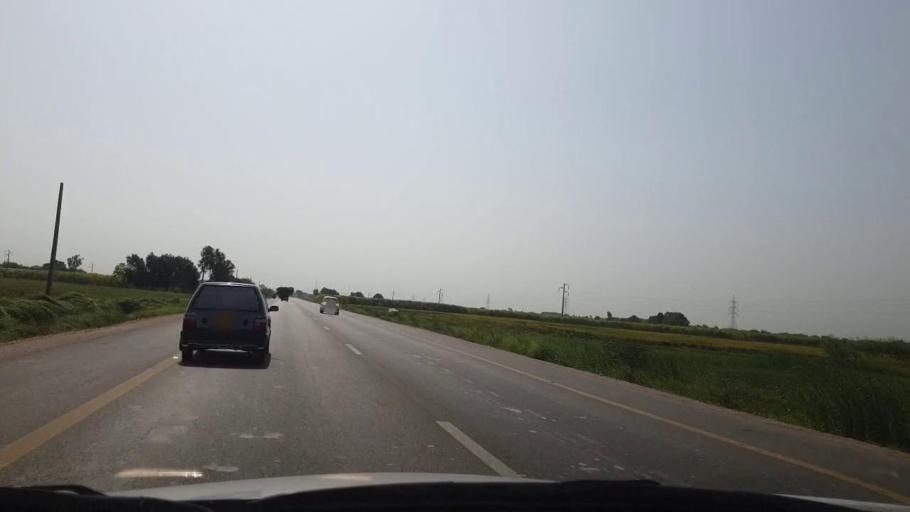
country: PK
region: Sindh
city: Tando Muhammad Khan
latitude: 25.1119
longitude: 68.5792
